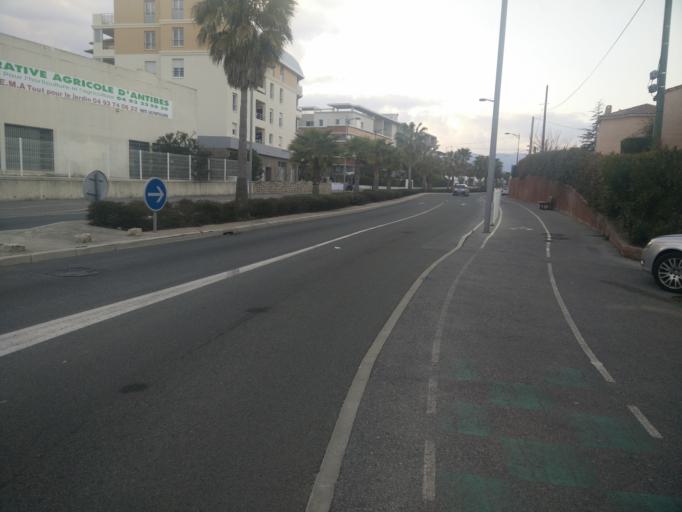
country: FR
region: Provence-Alpes-Cote d'Azur
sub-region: Departement des Alpes-Maritimes
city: Antibes
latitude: 43.5952
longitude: 7.1149
